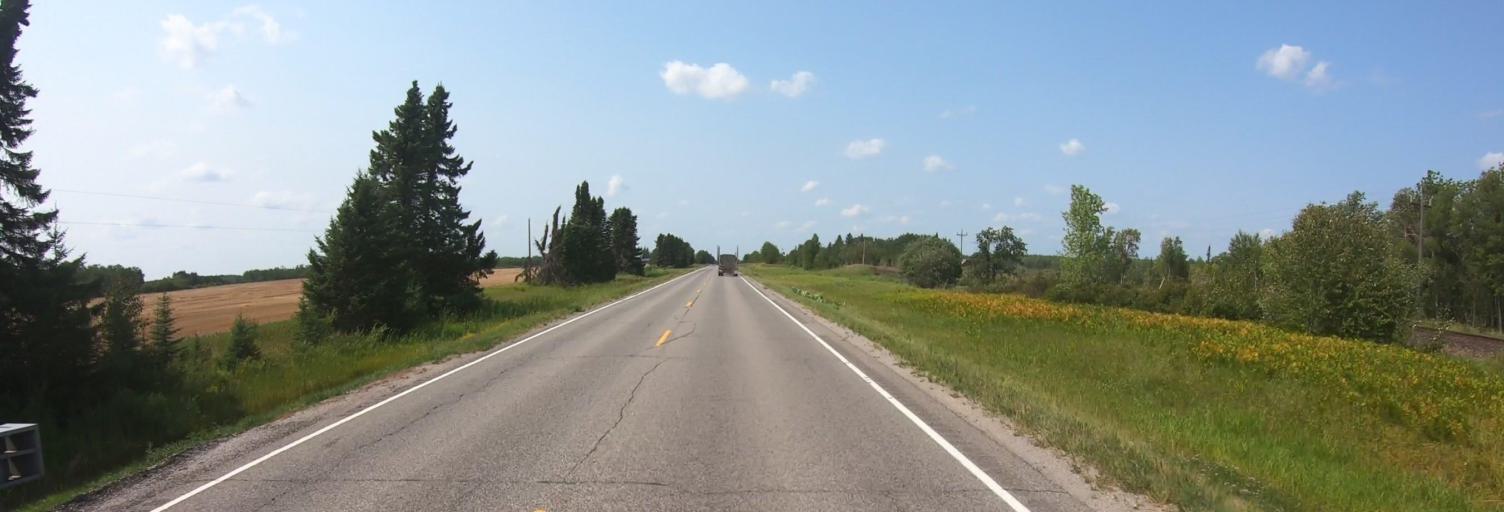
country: US
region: Minnesota
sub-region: Roseau County
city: Warroad
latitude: 48.8220
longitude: -95.1452
